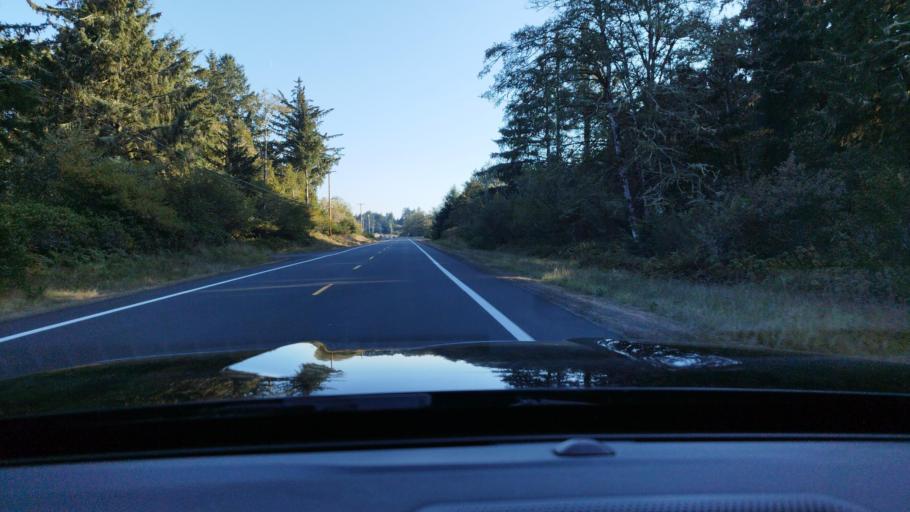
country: US
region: Oregon
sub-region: Clatsop County
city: Warrenton
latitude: 46.1690
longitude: -123.9493
